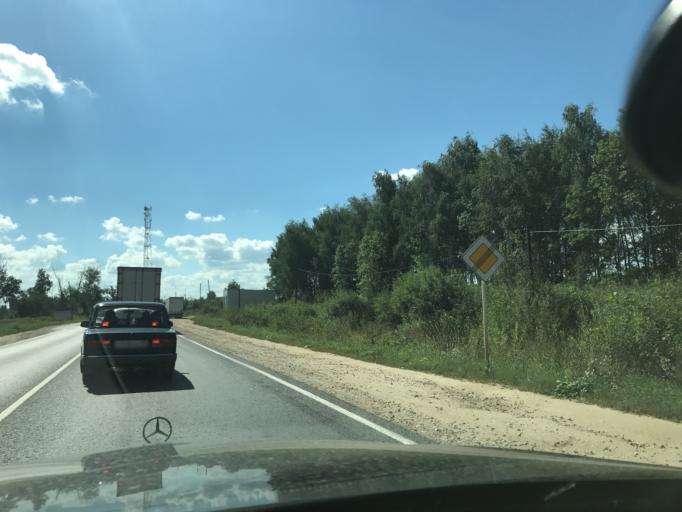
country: RU
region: Vladimir
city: Vorsha
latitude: 56.0626
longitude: 40.1218
